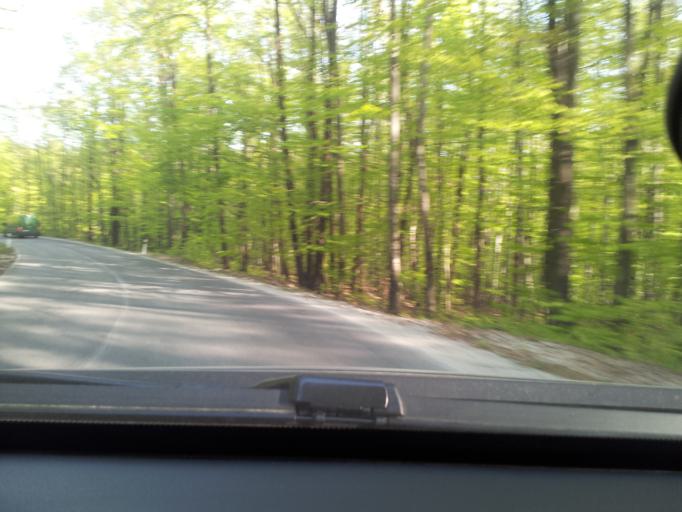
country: SK
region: Nitriansky
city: Partizanske
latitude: 48.5190
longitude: 18.3816
